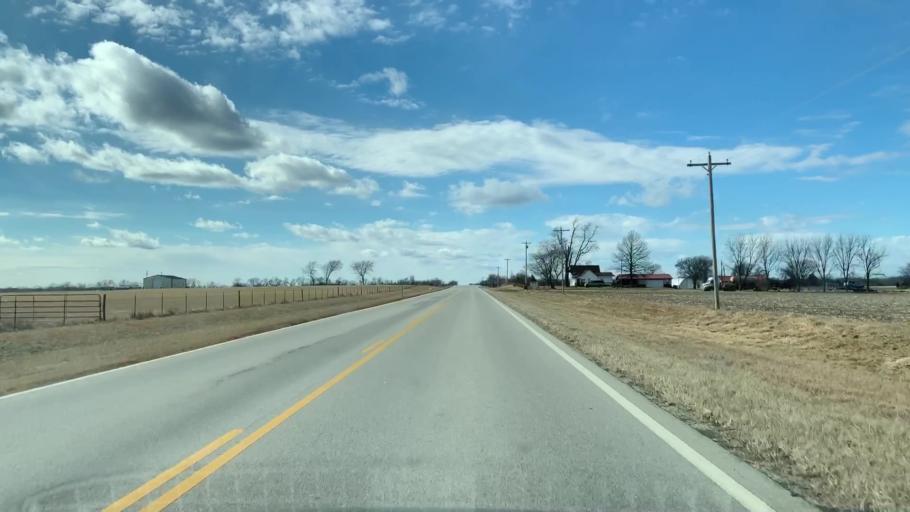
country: US
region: Kansas
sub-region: Neosho County
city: Chanute
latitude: 37.5290
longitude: -95.4115
